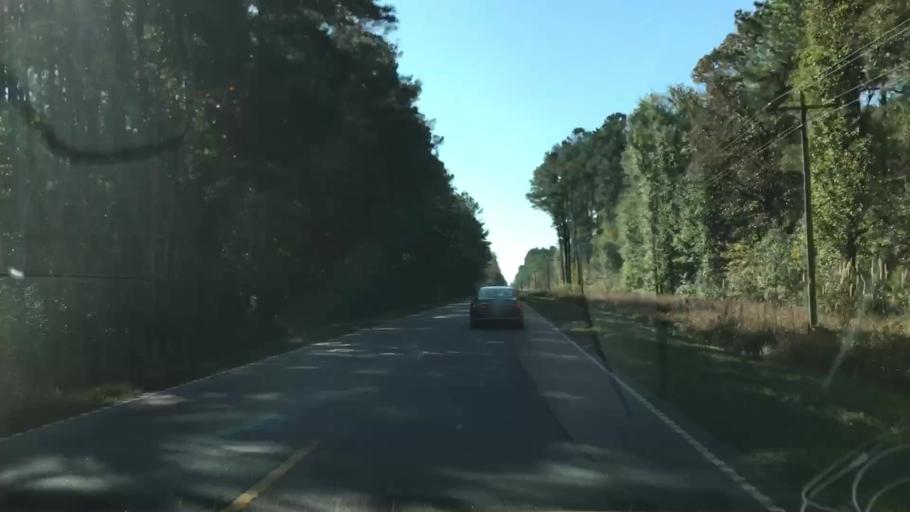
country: US
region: South Carolina
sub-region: Jasper County
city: Ridgeland
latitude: 32.3749
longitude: -80.9134
